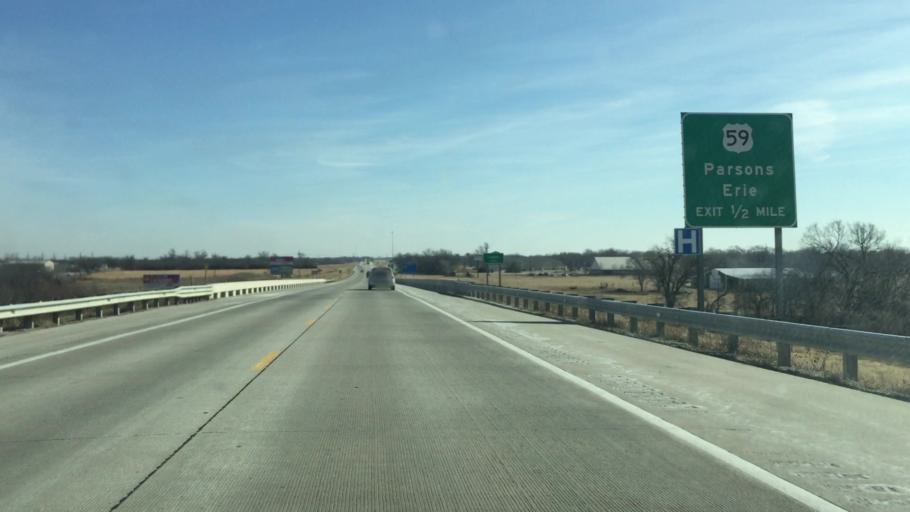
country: US
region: Kansas
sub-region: Labette County
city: Parsons
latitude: 37.3687
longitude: -95.2720
